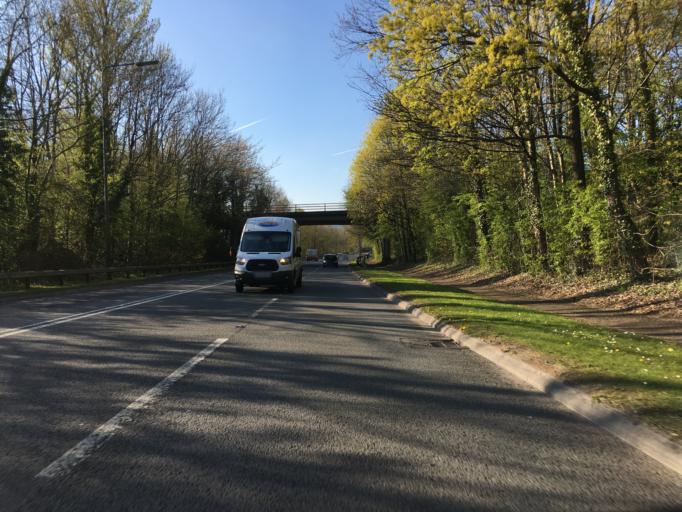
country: GB
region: Wales
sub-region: Torfaen County Borough
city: Cwmbran
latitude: 51.6246
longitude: -3.0139
